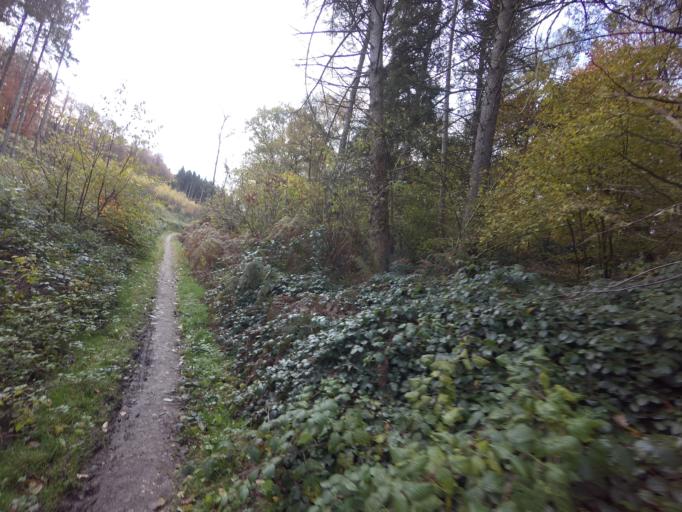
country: BE
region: Flanders
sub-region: Provincie Limburg
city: Sint-Pieters-Voeren
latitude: 50.7788
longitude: 5.8856
